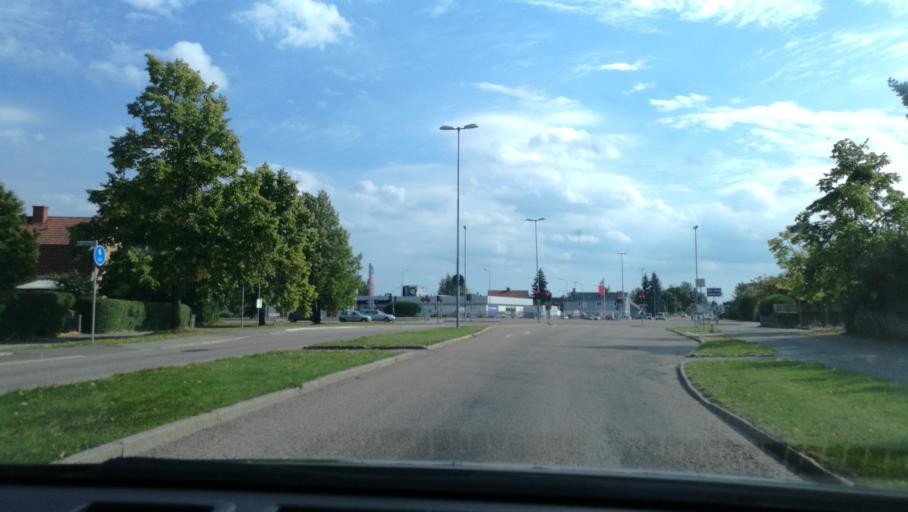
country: SE
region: Vaestmanland
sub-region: Vasteras
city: Vasteras
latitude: 59.6015
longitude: 16.5198
